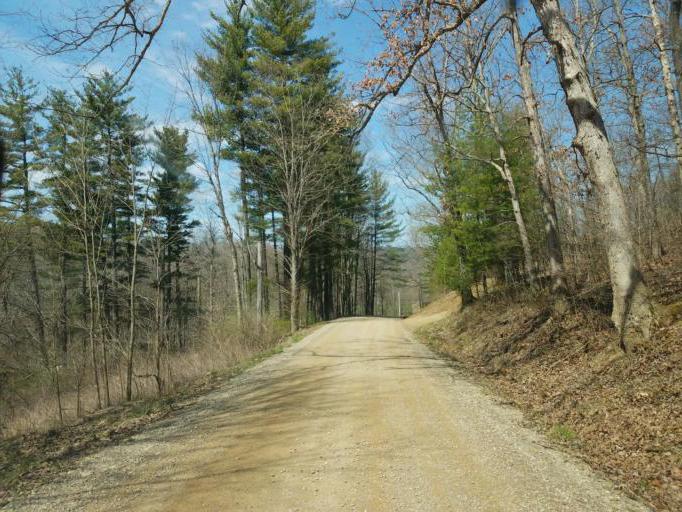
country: US
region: Ohio
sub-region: Knox County
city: Oak Hill
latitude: 40.3706
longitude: -82.2244
